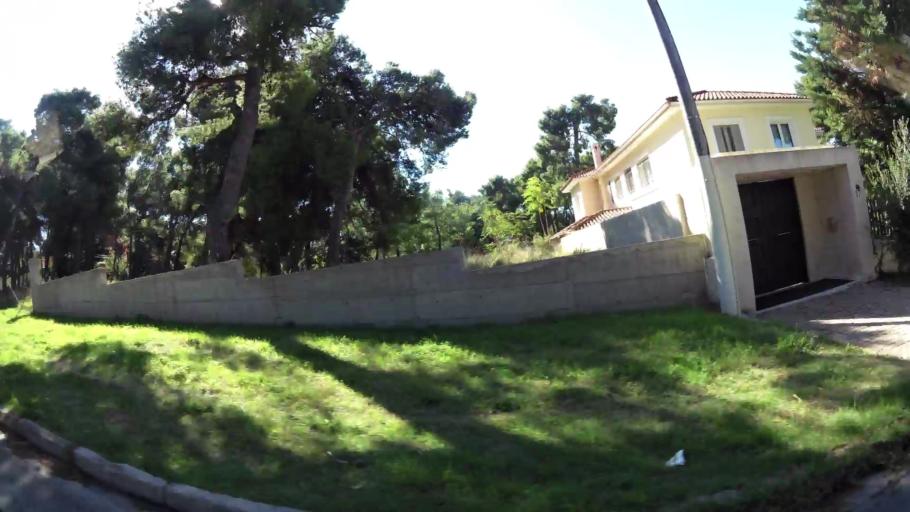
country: GR
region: Attica
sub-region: Nomarchia Athinas
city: Ekali
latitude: 38.1149
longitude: 23.8375
